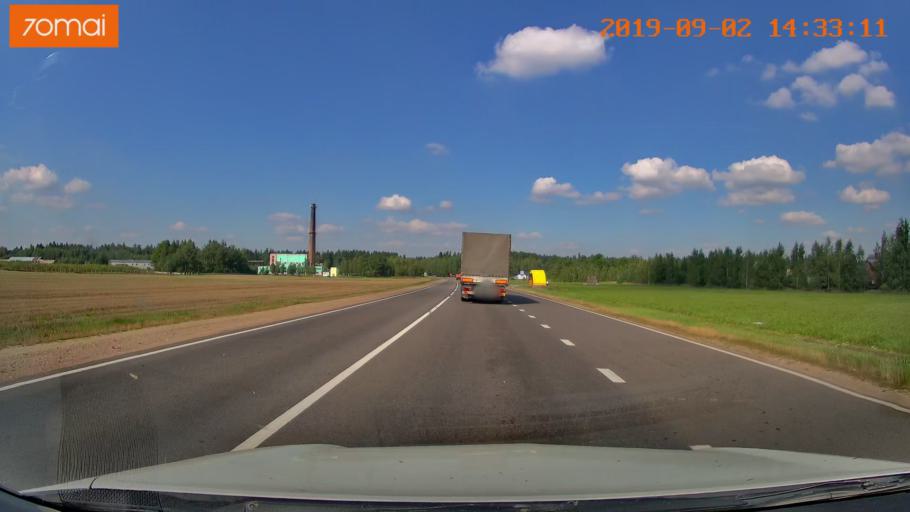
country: BY
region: Mogilev
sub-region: Mahilyowski Rayon
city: Kadino
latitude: 53.8813
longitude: 30.4892
